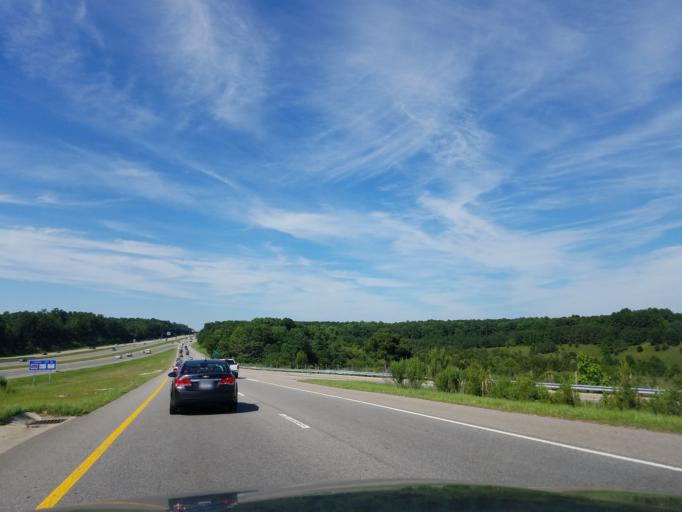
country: US
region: North Carolina
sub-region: Wake County
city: Morrisville
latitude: 35.8742
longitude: -78.8290
